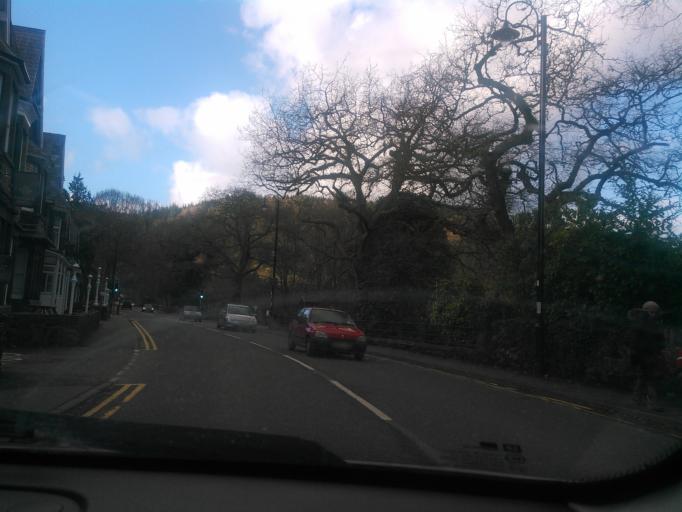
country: GB
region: Wales
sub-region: Conwy
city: Betws-y-Coed
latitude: 53.0910
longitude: -3.8007
